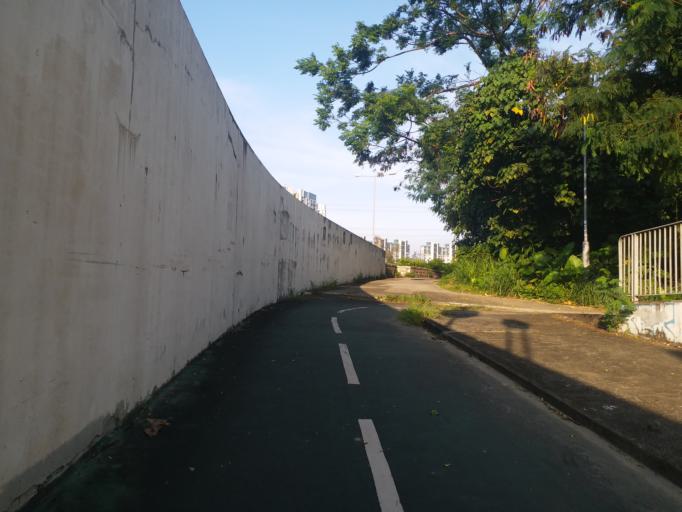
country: HK
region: Yuen Long
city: Yuen Long Kau Hui
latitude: 22.4440
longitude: 114.0481
